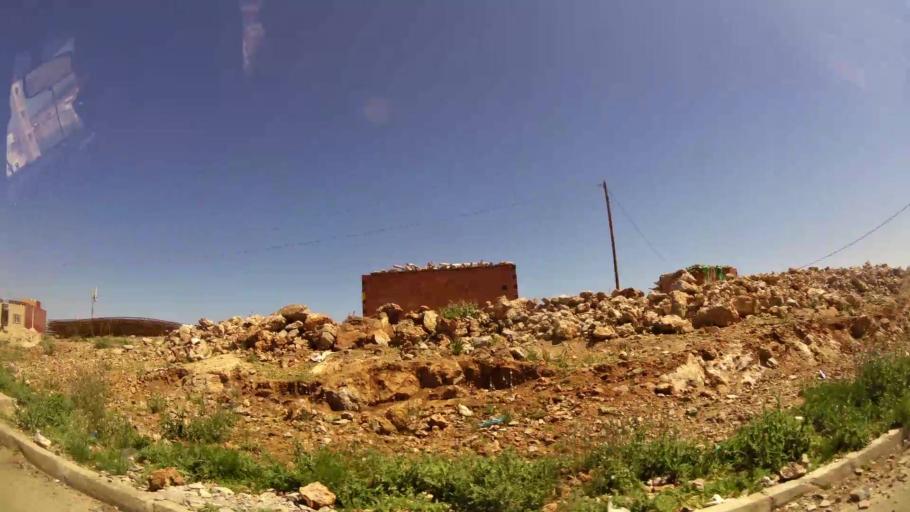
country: MA
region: Oriental
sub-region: Oujda-Angad
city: Oujda
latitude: 34.6516
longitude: -1.8704
